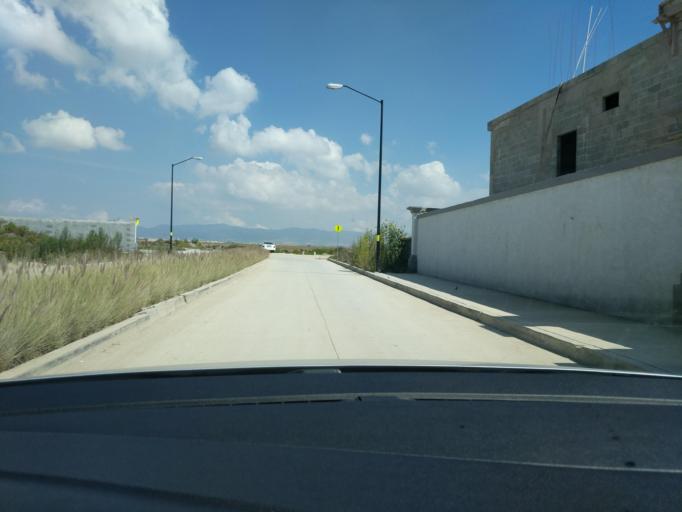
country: MX
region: Hidalgo
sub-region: Zempoala
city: Jagueey de Tellez (Estacion Tellez)
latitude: 20.0061
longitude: -98.7739
